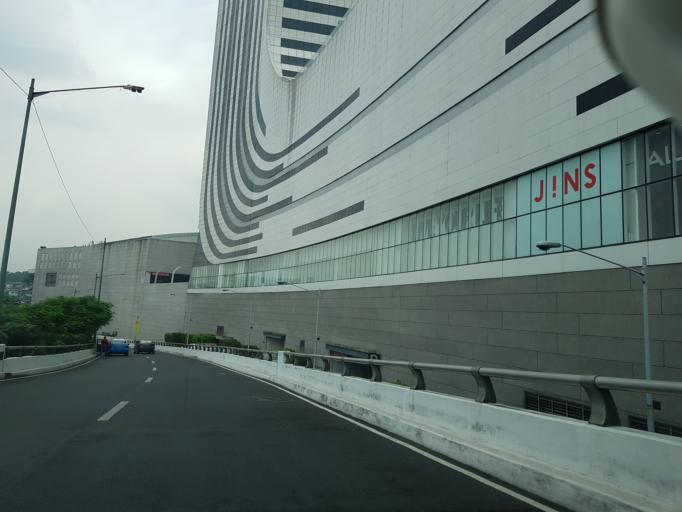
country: PH
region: Calabarzon
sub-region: Province of Rizal
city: Pateros
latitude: 14.5459
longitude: 121.0544
